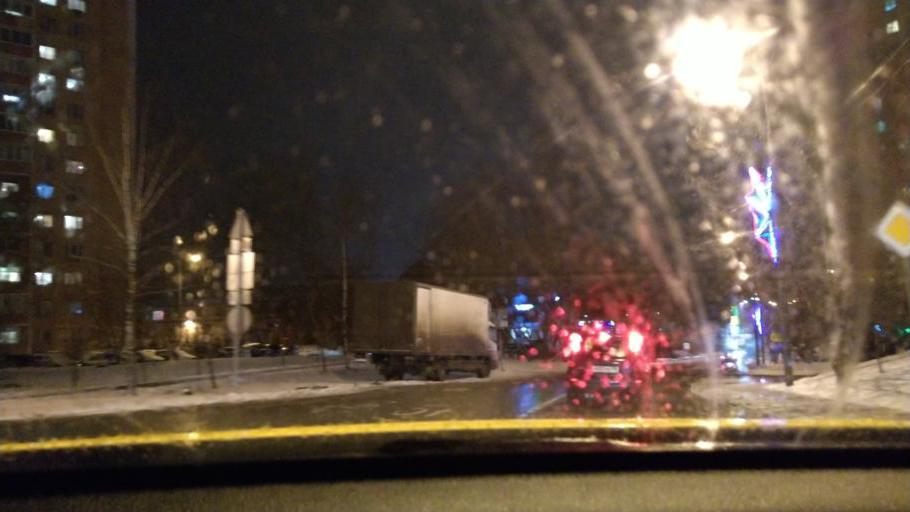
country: RU
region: Moskovskaya
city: Troitsk
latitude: 55.4914
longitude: 37.2991
